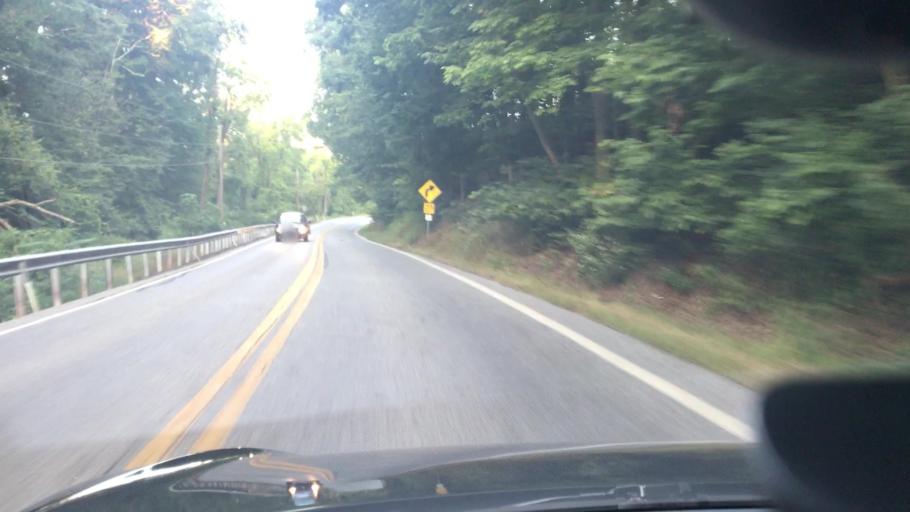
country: US
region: Pennsylvania
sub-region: Cumberland County
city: Lower Allen
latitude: 40.1630
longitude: -76.8928
